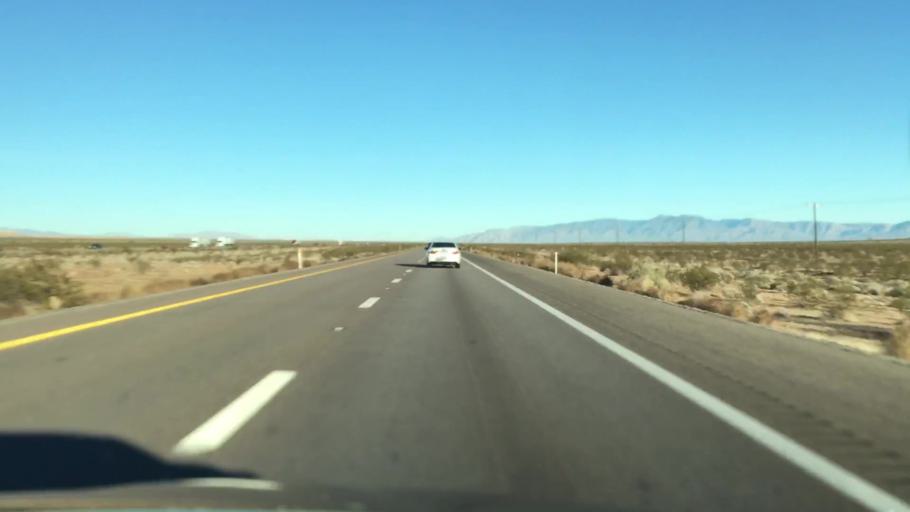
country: US
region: Nevada
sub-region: Clark County
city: Moapa Valley
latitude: 36.7497
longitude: -114.4014
